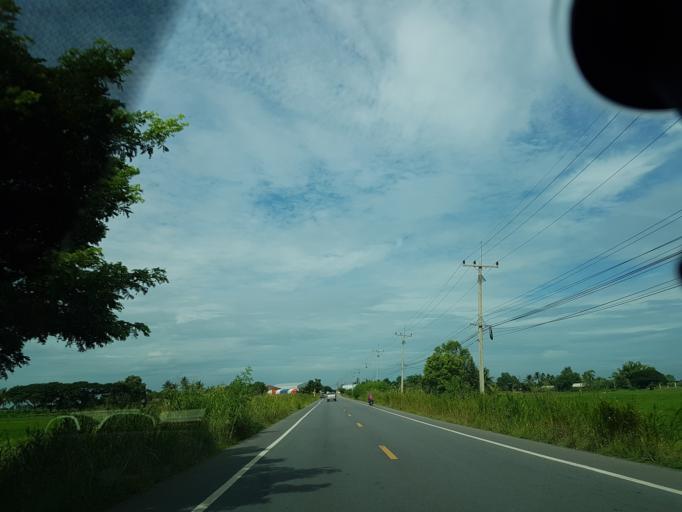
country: TH
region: Lop Buri
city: Tha Wung
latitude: 14.7546
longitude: 100.5562
